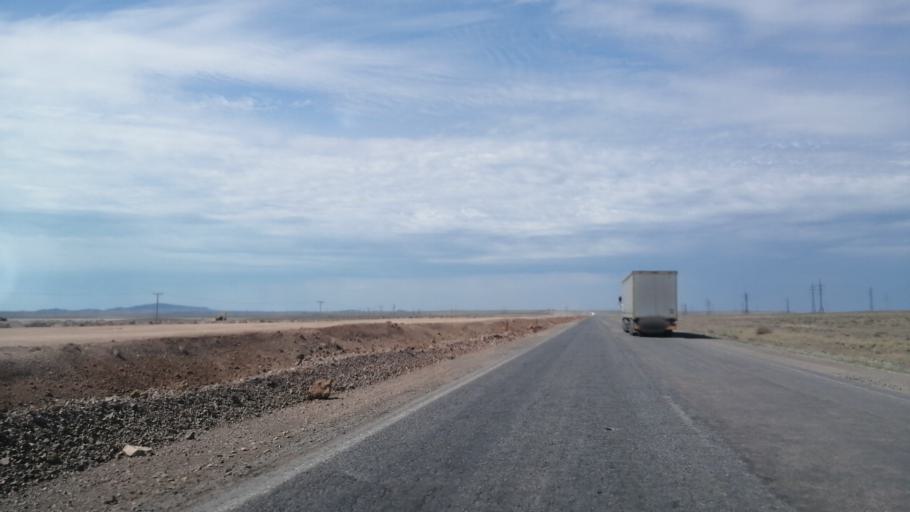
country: KZ
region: Qaraghandy
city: Balqash
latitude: 46.7316
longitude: 74.5045
